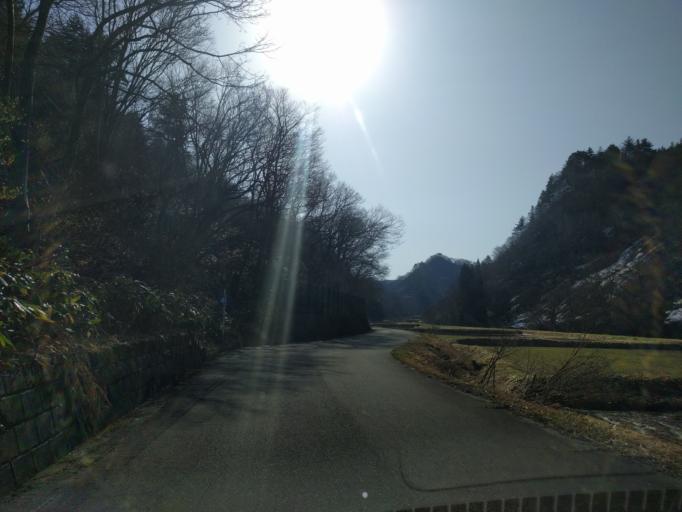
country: JP
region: Niigata
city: Muramatsu
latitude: 37.3637
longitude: 139.4559
